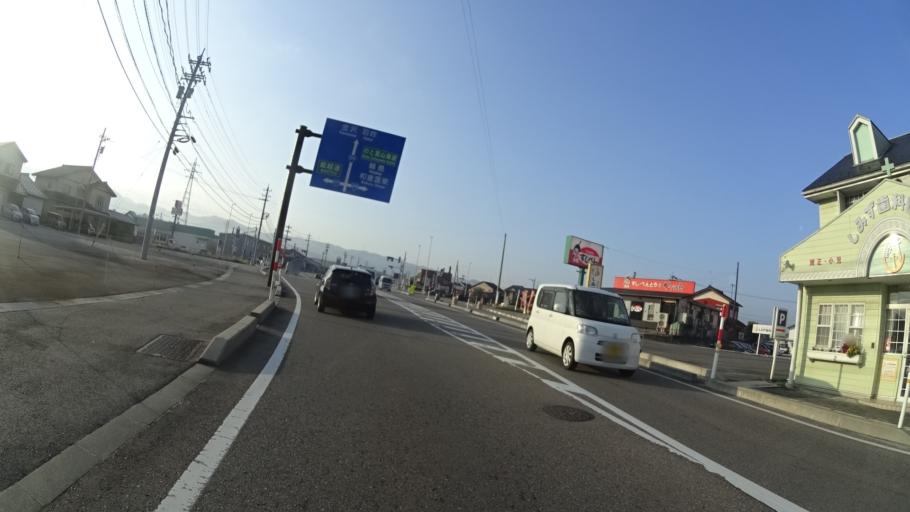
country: JP
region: Ishikawa
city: Nanao
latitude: 37.0326
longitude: 136.9676
